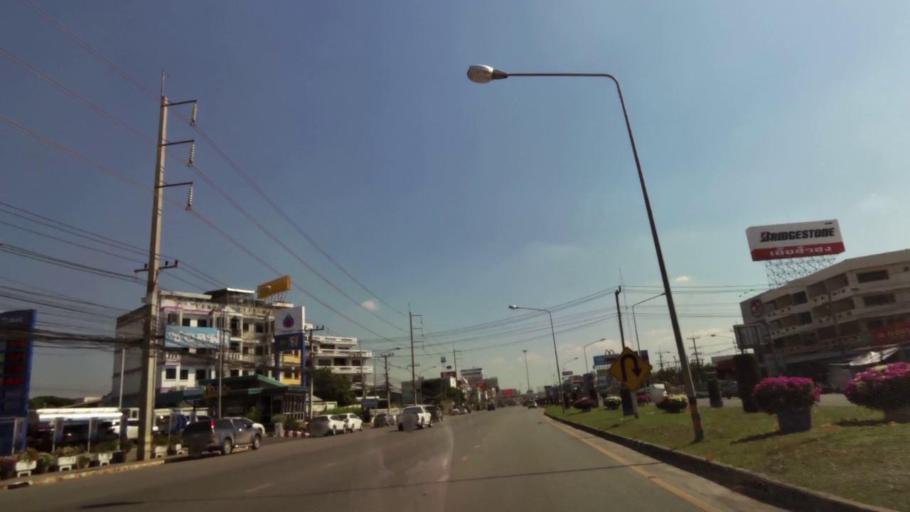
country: TH
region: Nakhon Sawan
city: Nakhon Sawan
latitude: 15.7032
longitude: 100.1154
